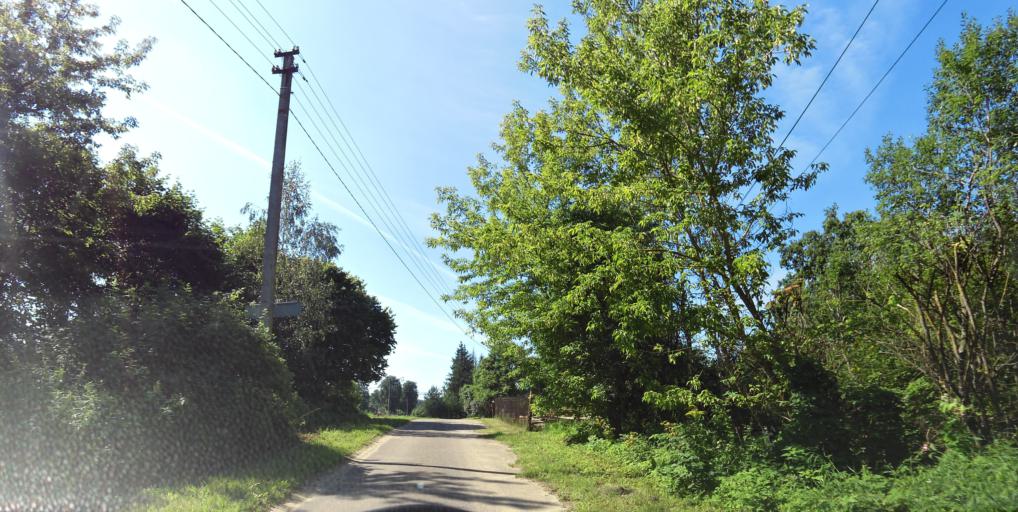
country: LT
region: Vilnius County
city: Rasos
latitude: 54.6801
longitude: 25.3577
